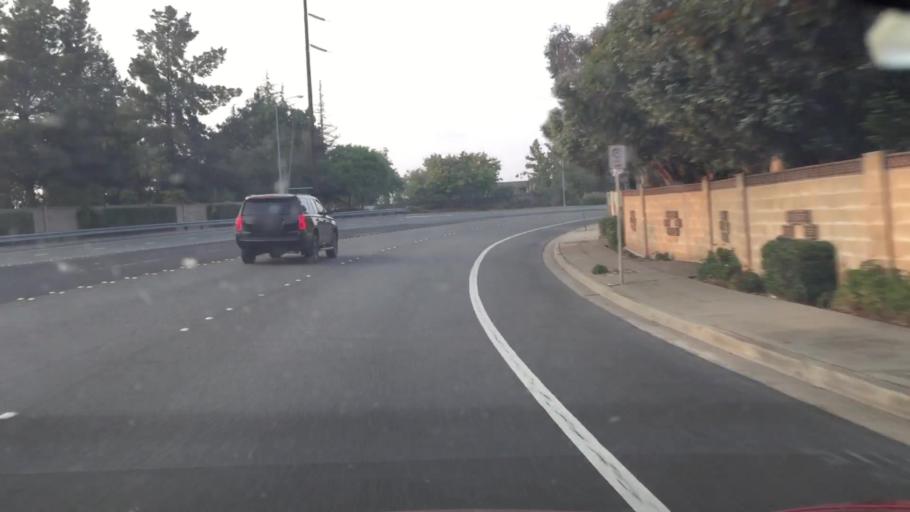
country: US
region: California
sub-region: Alameda County
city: Livermore
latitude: 37.6580
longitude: -121.7829
